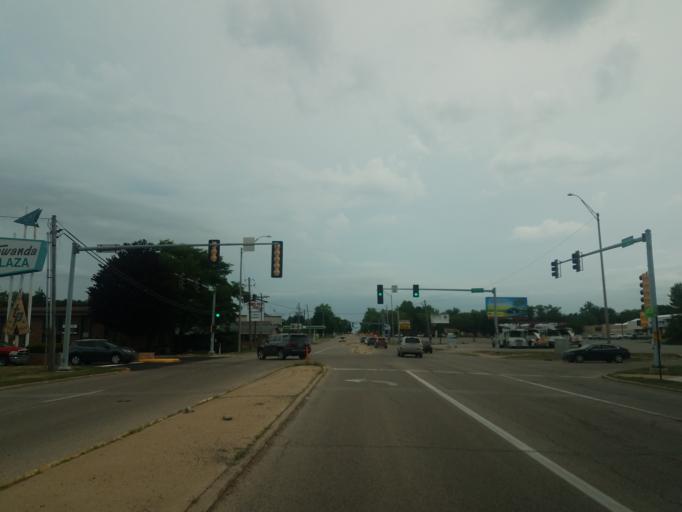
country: US
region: Illinois
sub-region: McLean County
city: Bloomington
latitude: 40.4894
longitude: -88.9690
